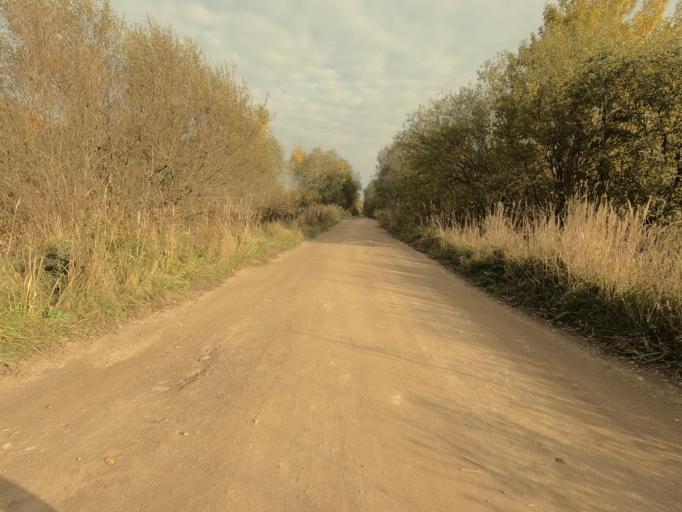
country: RU
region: Novgorod
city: Volkhovskiy
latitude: 58.8937
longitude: 31.0193
